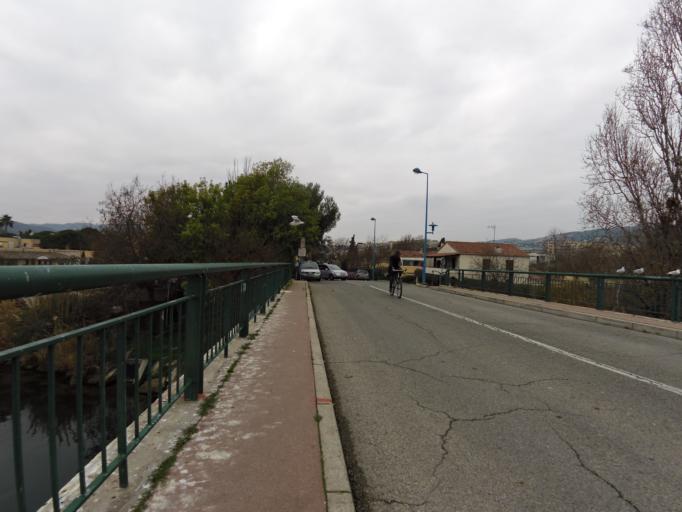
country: FR
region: Provence-Alpes-Cote d'Azur
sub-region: Departement des Alpes-Maritimes
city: Mandelieu-la-Napoule
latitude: 43.5352
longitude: 6.9441
